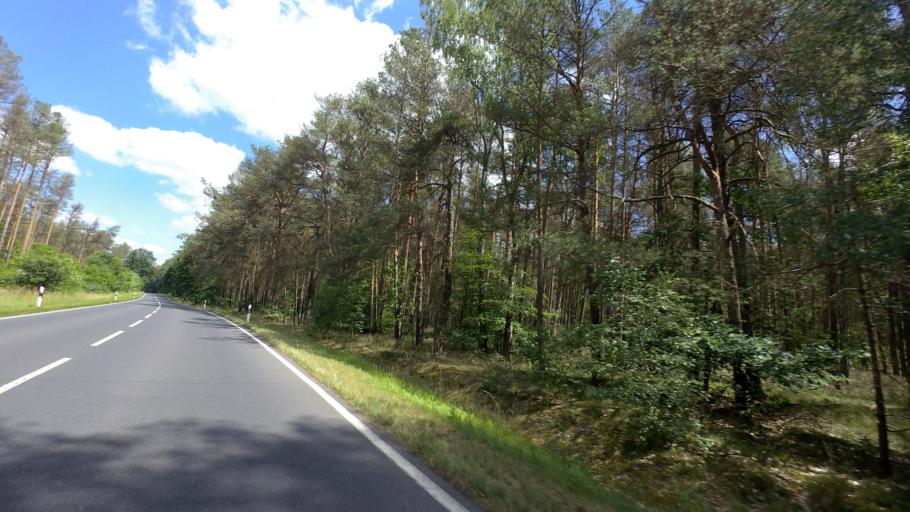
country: DE
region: Brandenburg
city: Sonnewalde
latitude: 51.7354
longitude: 13.6806
